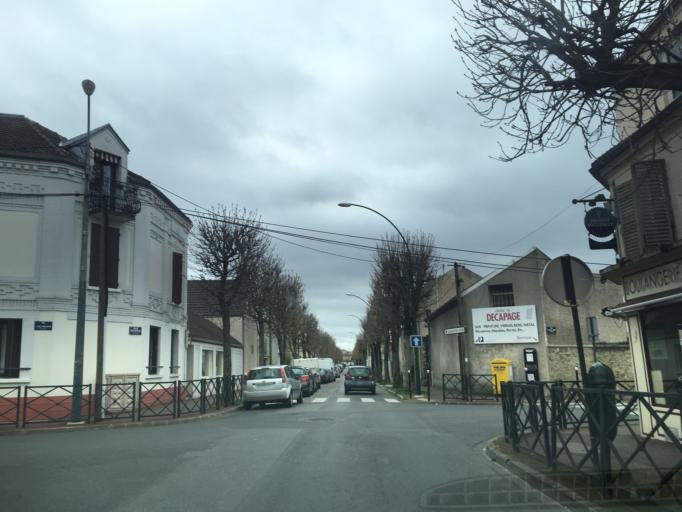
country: FR
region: Ile-de-France
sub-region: Departement du Val-de-Marne
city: Saint-Maur-des-Fosses
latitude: 48.7912
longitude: 2.4906
